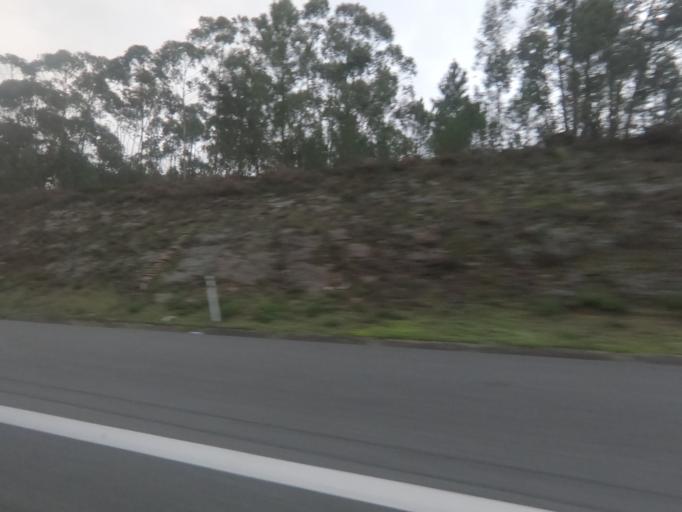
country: PT
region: Viana do Castelo
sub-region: Ponte de Lima
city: Ponte de Lima
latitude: 41.7532
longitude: -8.5565
